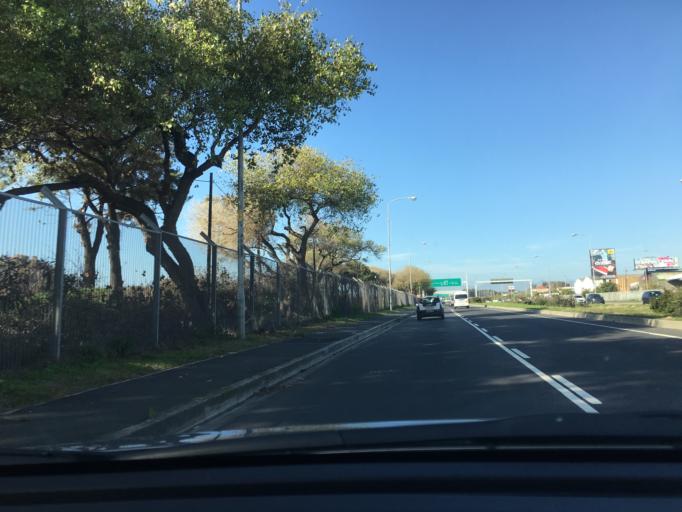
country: ZA
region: Western Cape
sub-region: City of Cape Town
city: Lansdowne
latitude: -33.9678
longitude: 18.5797
